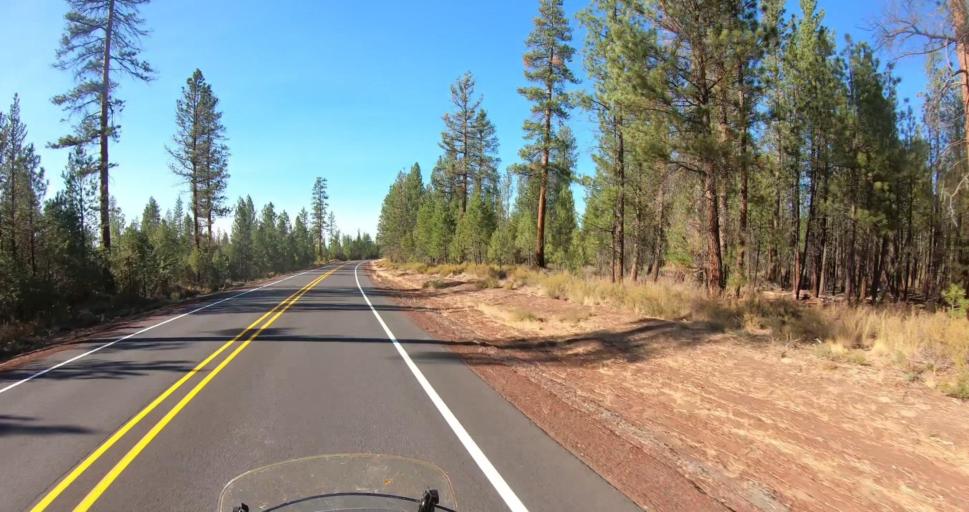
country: US
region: Oregon
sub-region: Deschutes County
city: La Pine
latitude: 43.4944
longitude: -121.4447
